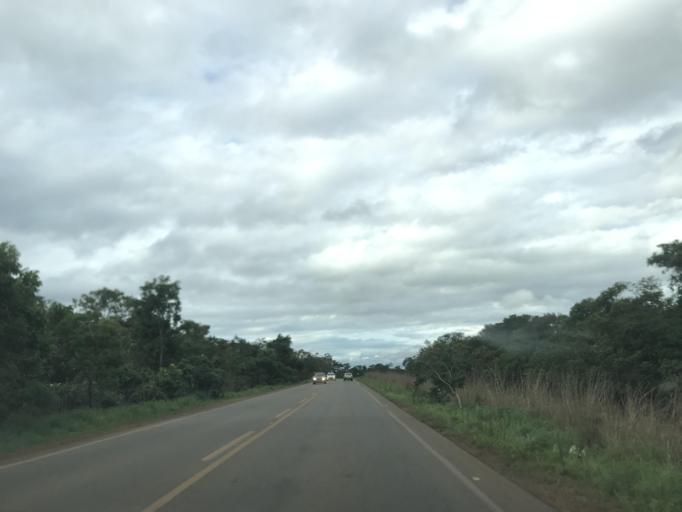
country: BR
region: Goias
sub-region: Vianopolis
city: Vianopolis
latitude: -16.7362
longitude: -48.4465
